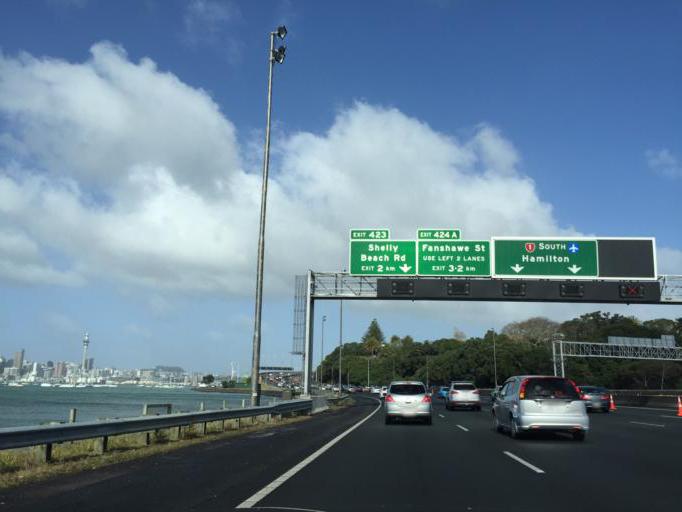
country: NZ
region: Auckland
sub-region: Auckland
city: North Shore
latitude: -36.8190
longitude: 174.7503
